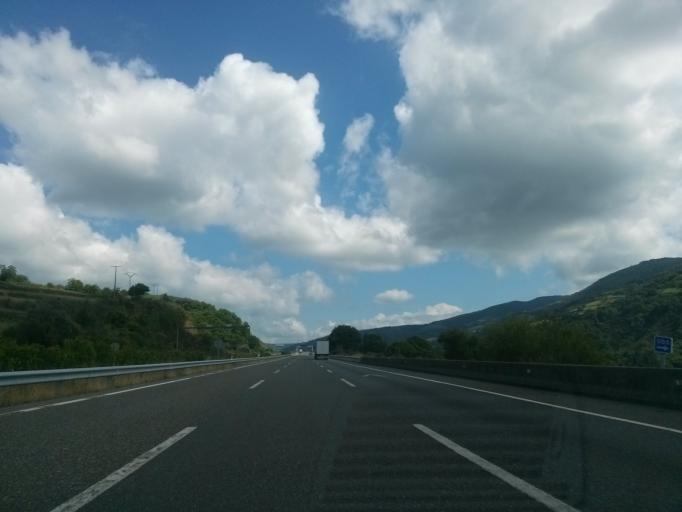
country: ES
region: Galicia
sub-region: Provincia de Lugo
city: San Roman
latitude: 42.7802
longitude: -7.1004
